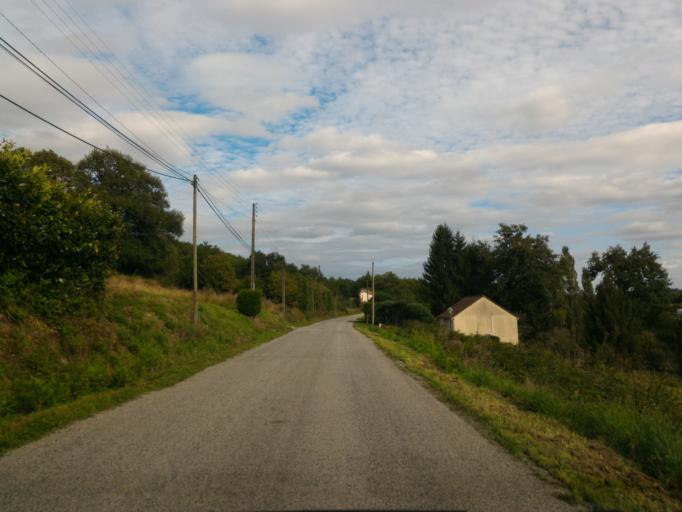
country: FR
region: Limousin
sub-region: Departement de la Haute-Vienne
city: Saint-Junien
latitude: 45.8968
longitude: 0.8773
